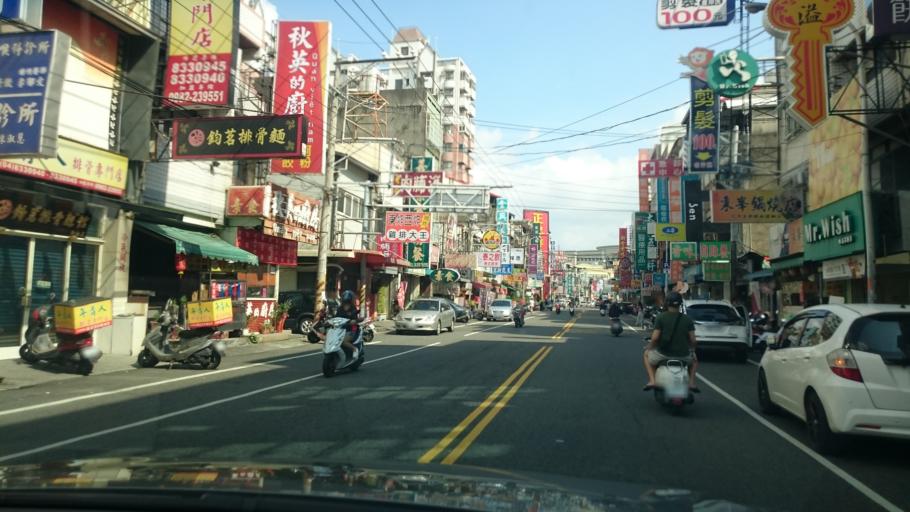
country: TW
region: Taiwan
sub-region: Nantou
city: Nantou
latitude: 23.9542
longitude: 120.5746
